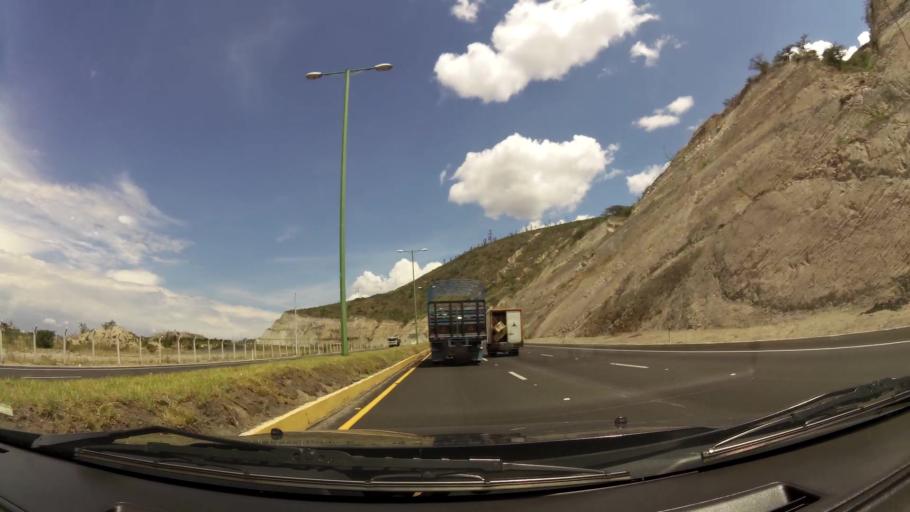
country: EC
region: Pichincha
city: Quito
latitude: -0.0881
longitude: -78.4015
